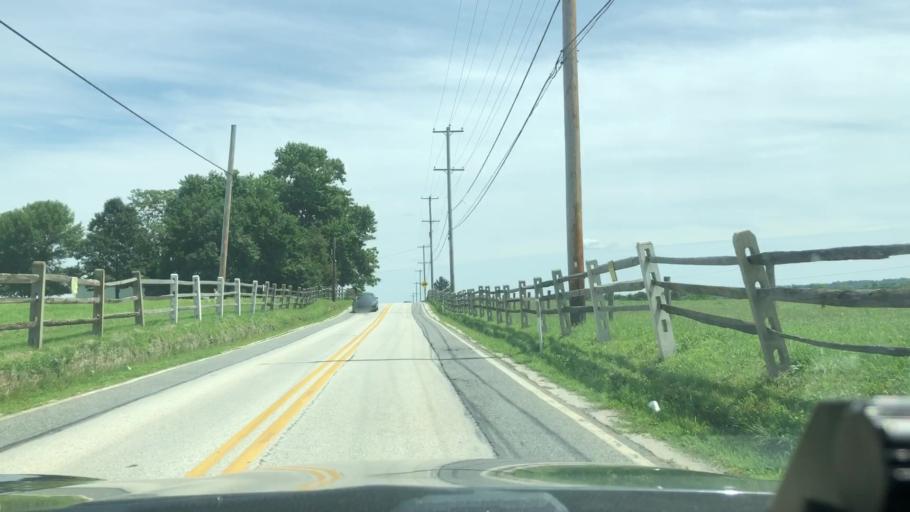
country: US
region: Pennsylvania
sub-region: Montgomery County
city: Plymouth Meeting
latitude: 40.1014
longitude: -75.2463
